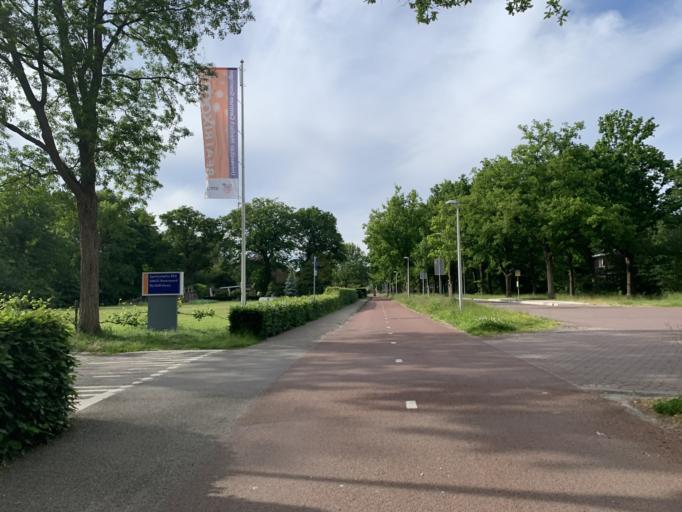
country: NL
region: Groningen
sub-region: Gemeente Haren
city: Haren
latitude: 53.1828
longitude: 6.6023
